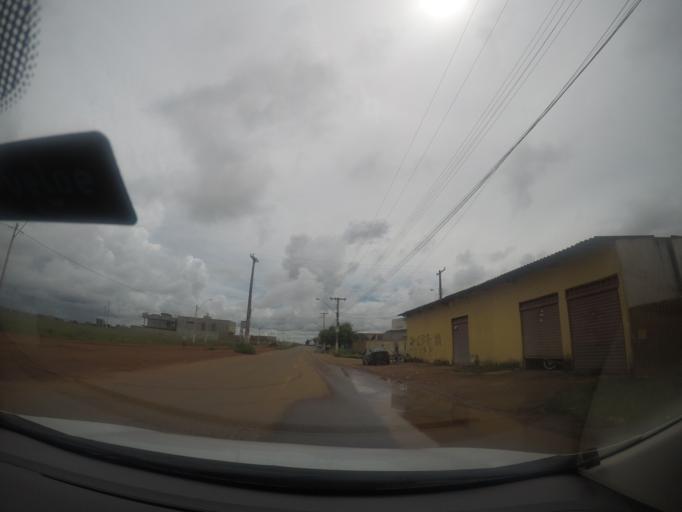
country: BR
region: Goias
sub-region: Trindade
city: Trindade
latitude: -16.6972
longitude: -49.4097
